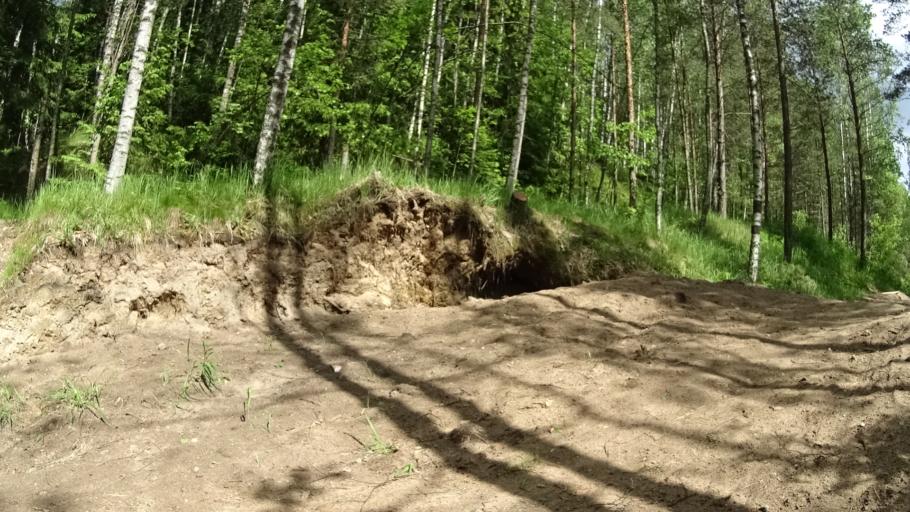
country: FI
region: Uusimaa
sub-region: Helsinki
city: Espoo
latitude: 60.2012
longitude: 24.6328
